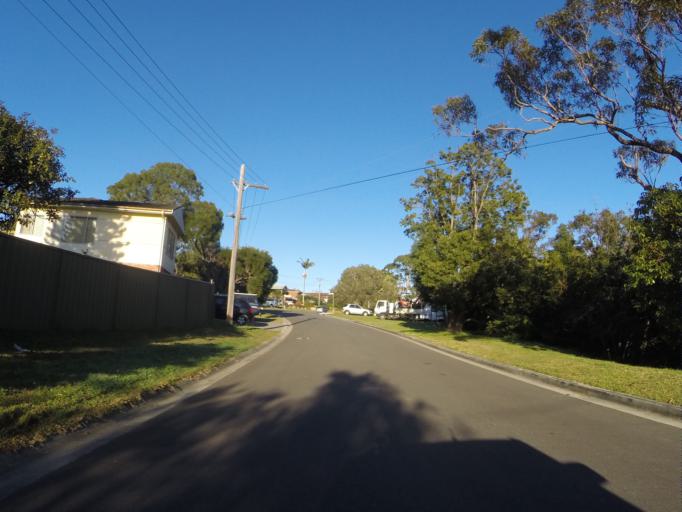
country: AU
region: New South Wales
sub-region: Sutherland Shire
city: Loftus
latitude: -34.0404
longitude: 151.0442
